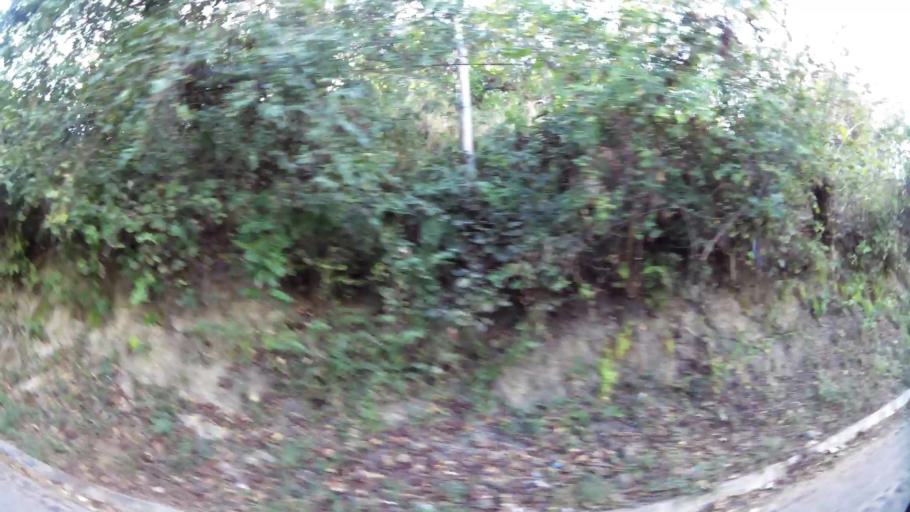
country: SV
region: Cuscatlan
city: Suchitoto
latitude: 13.9441
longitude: -89.0162
